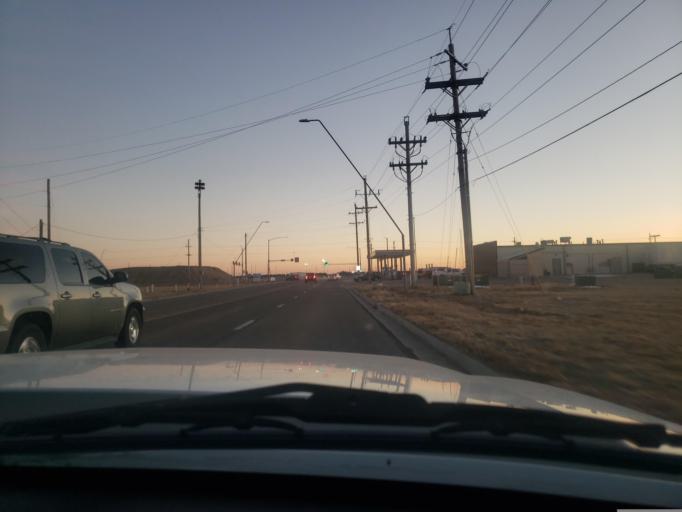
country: US
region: Kansas
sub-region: Finney County
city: Garden City
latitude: 37.9618
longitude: -100.8291
